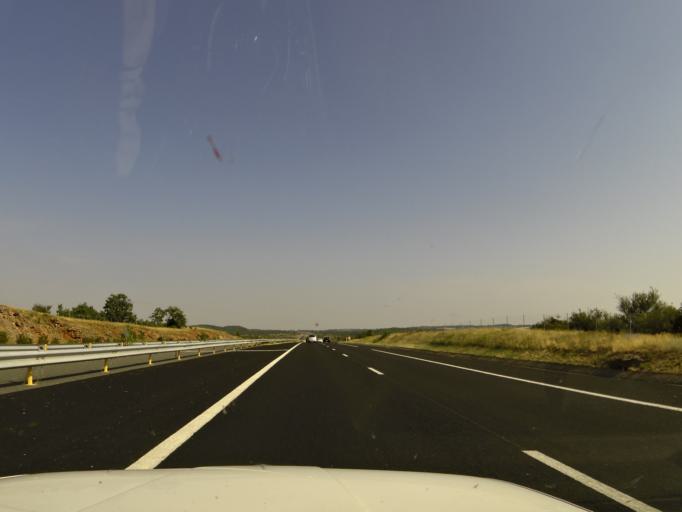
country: FR
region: Midi-Pyrenees
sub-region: Departement de l'Aveyron
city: La Cavalerie
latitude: 43.9458
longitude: 3.2207
